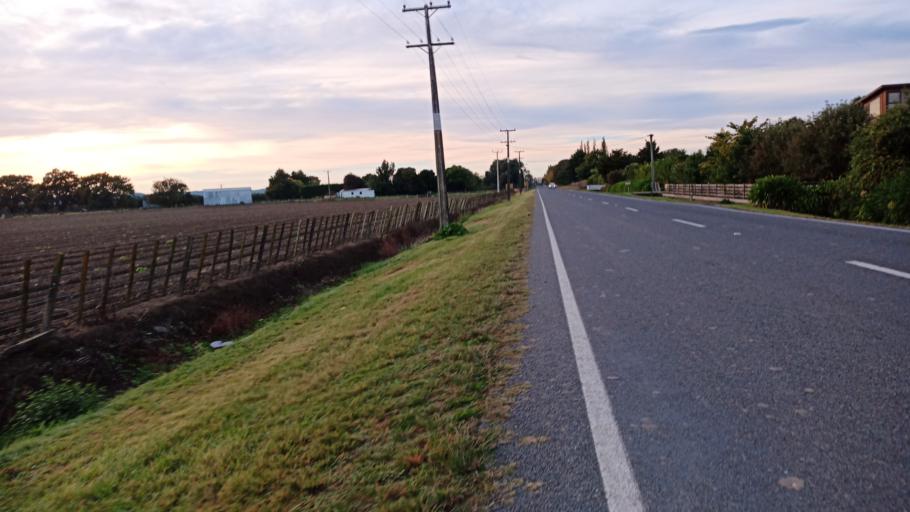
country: NZ
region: Gisborne
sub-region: Gisborne District
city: Gisborne
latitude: -38.6430
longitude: 177.9390
